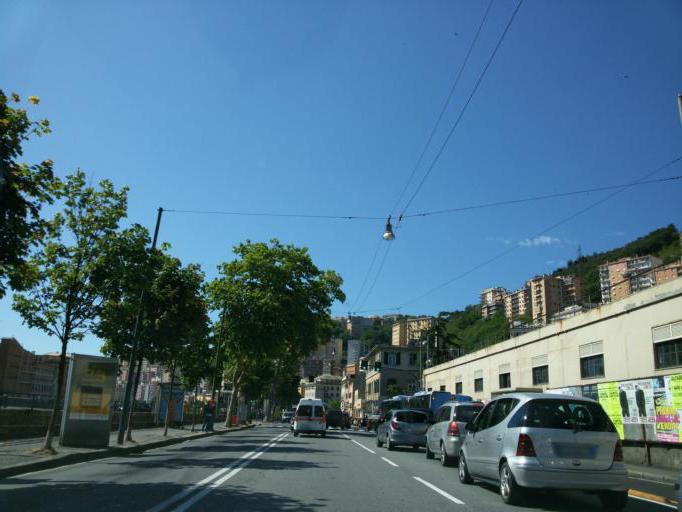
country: IT
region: Liguria
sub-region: Provincia di Genova
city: Genoa
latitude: 44.4236
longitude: 8.9471
